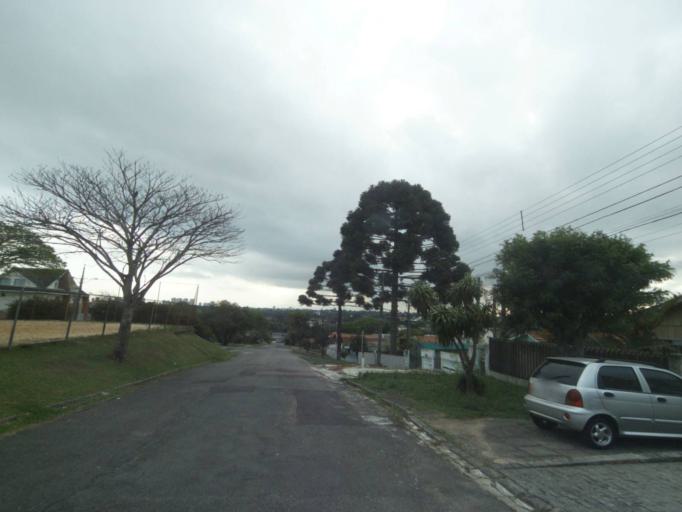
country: BR
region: Parana
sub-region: Pinhais
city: Pinhais
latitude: -25.4170
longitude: -49.2101
